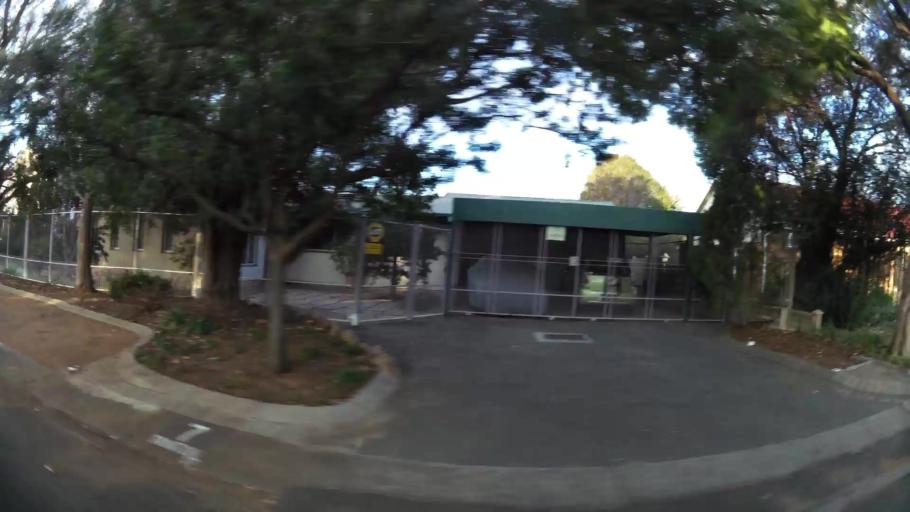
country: ZA
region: Orange Free State
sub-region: Mangaung Metropolitan Municipality
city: Bloemfontein
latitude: -29.1409
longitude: 26.1828
